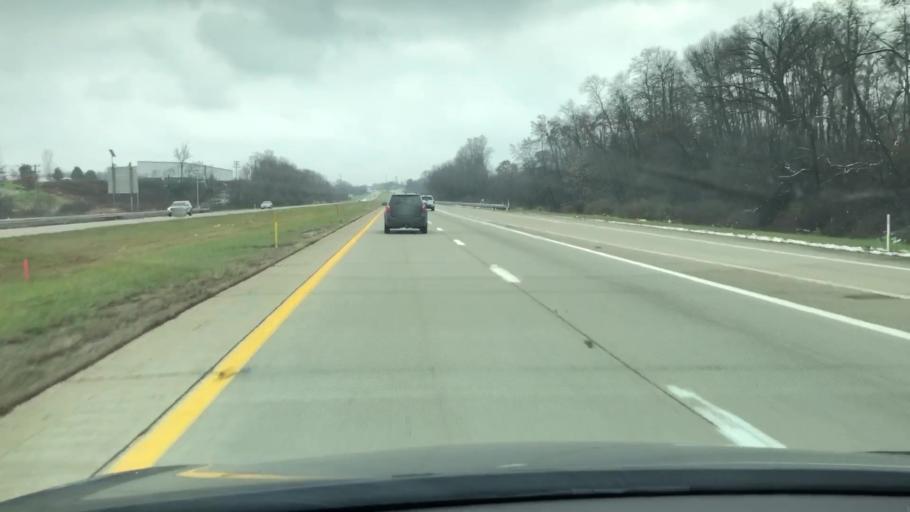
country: US
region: Pennsylvania
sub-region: Westmoreland County
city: New Stanton
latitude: 40.1931
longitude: -79.5712
